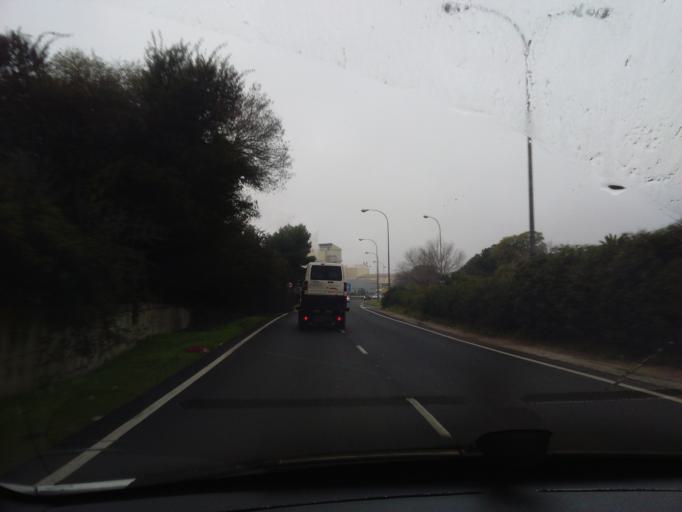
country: ES
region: Andalusia
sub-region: Provincia de Sevilla
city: Sevilla
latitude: 37.3869
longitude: -5.9228
